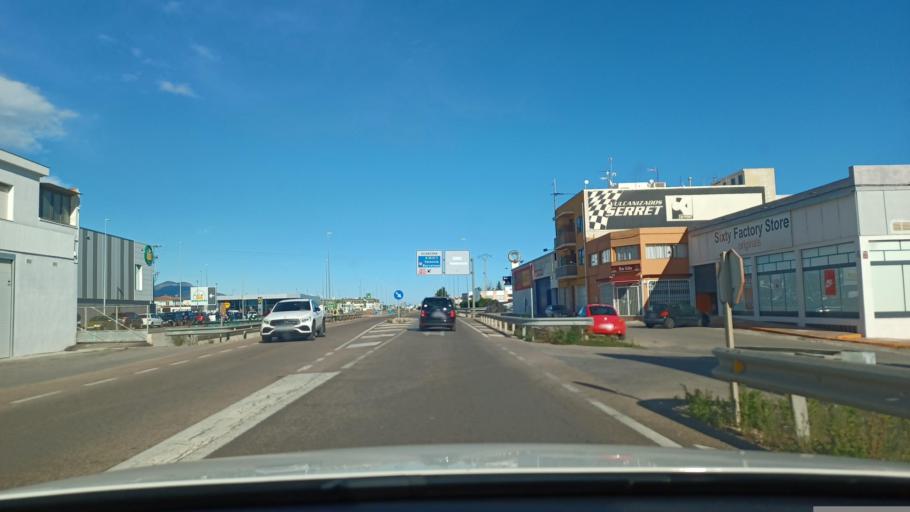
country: ES
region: Valencia
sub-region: Provincia de Castello
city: Vinaros
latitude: 40.4814
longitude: 0.4733
